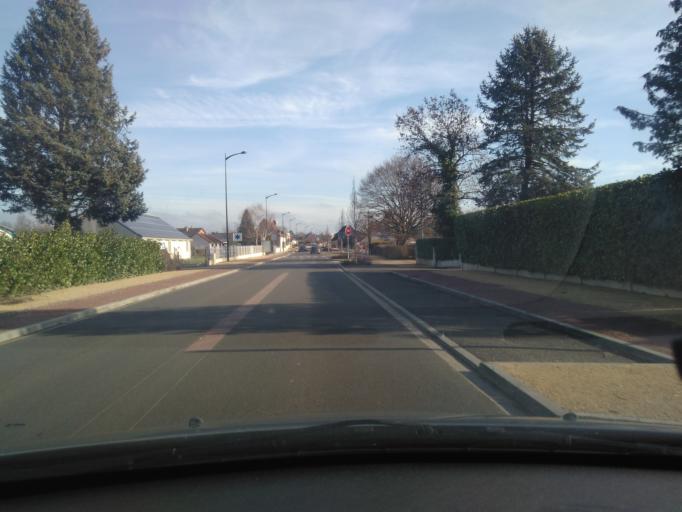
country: FR
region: Centre
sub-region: Departement du Cher
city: Saint-Amand-Montrond
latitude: 46.7213
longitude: 2.5244
